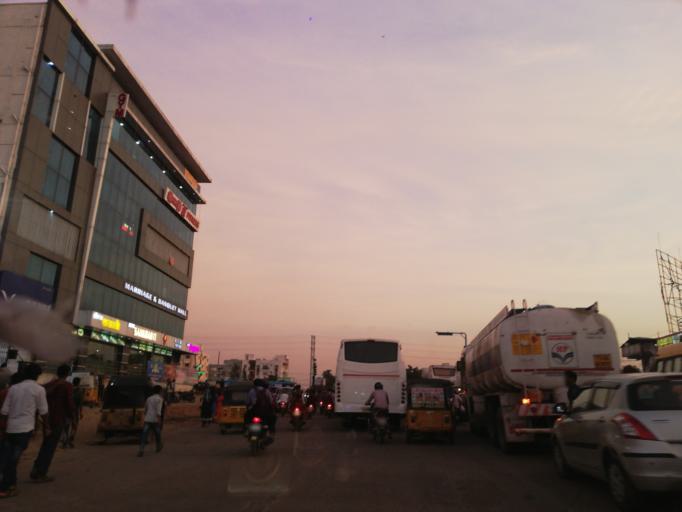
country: IN
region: Telangana
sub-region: Rangareddi
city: Kukatpalli
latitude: 17.4975
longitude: 78.3618
